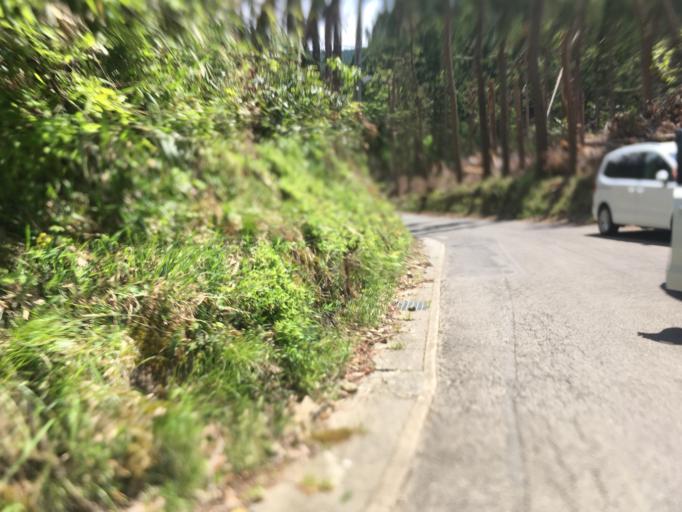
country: JP
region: Kyoto
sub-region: Kyoto-shi
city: Kamigyo-ku
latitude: 35.0997
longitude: 135.7421
